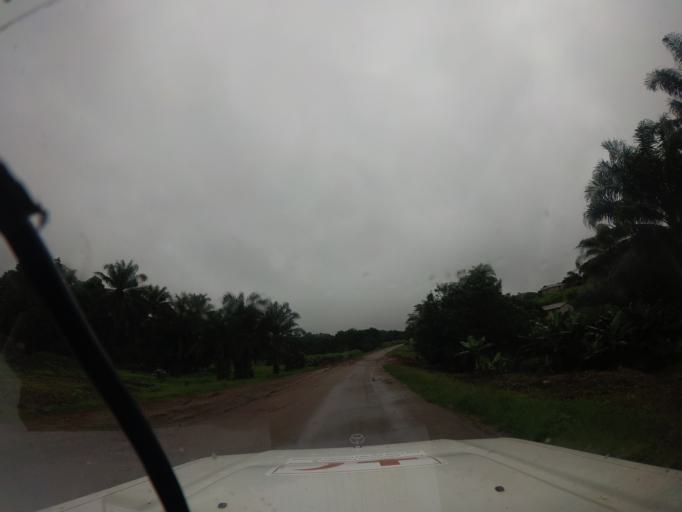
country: SL
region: Northern Province
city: Kabala
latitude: 9.5010
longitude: -11.5963
